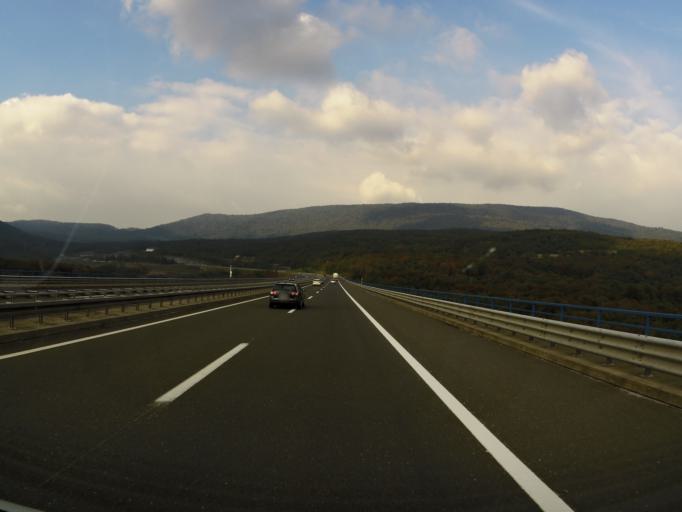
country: HR
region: Licko-Senjska
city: Brinje
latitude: 45.0584
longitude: 15.2034
